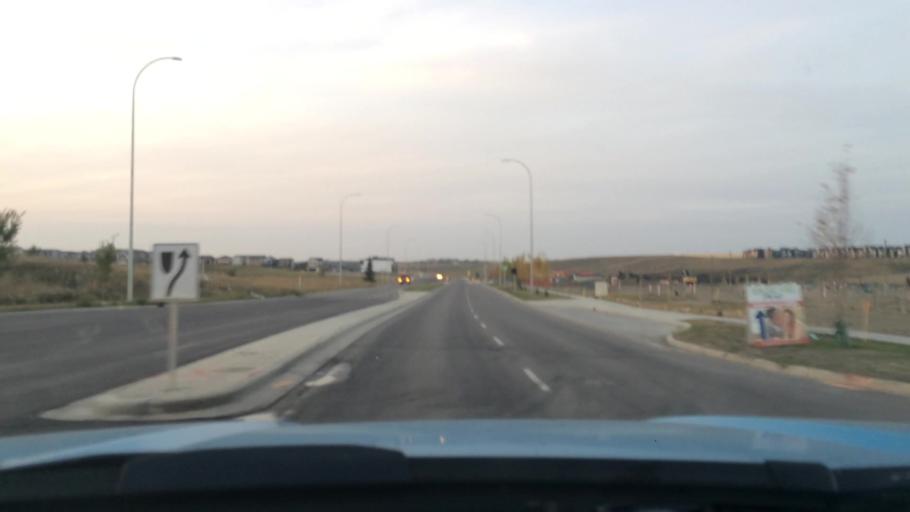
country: CA
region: Alberta
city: Calgary
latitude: 51.1731
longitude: -114.1337
